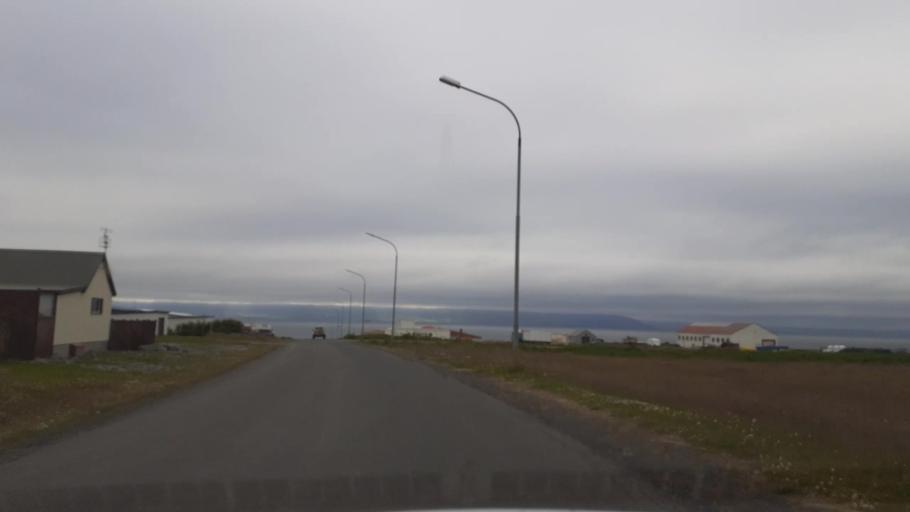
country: IS
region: Northwest
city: Saudarkrokur
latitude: 65.9009
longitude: -19.4192
